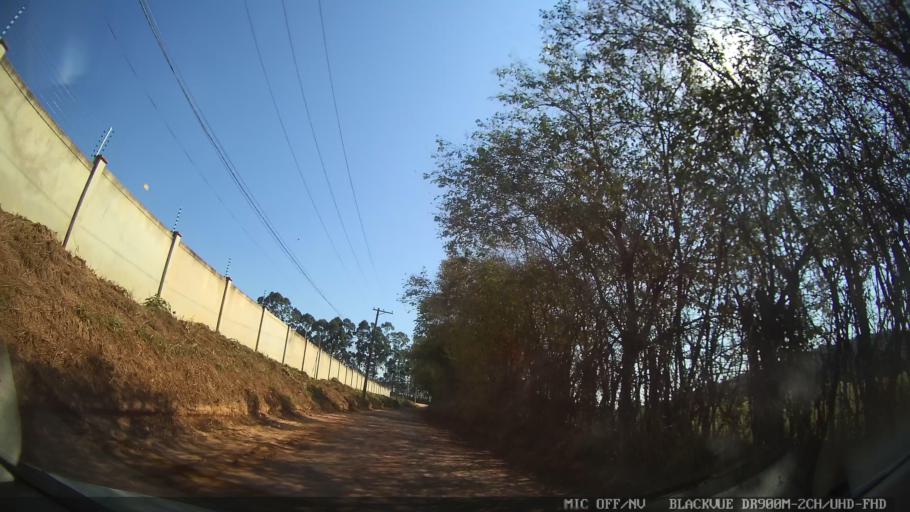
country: BR
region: Sao Paulo
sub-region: Itupeva
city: Itupeva
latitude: -23.1101
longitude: -47.0538
